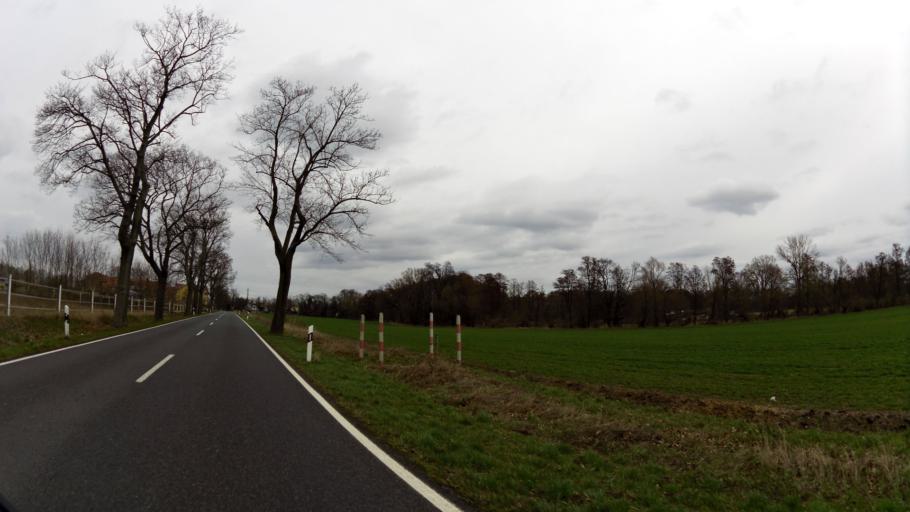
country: DE
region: Brandenburg
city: Schonefeld
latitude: 52.3391
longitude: 13.5047
